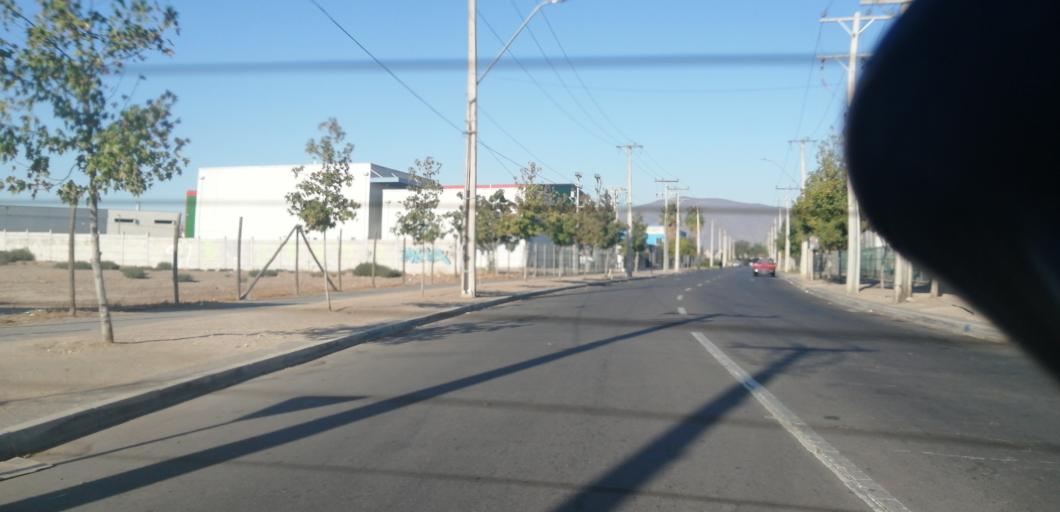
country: CL
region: Santiago Metropolitan
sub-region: Provincia de Santiago
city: Lo Prado
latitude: -33.4316
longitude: -70.7751
